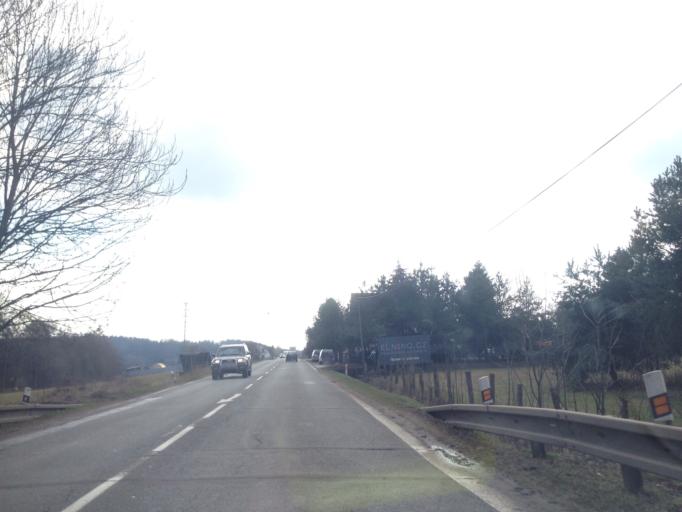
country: CZ
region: Kralovehradecky
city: Nova Paka
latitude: 50.4755
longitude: 15.5017
